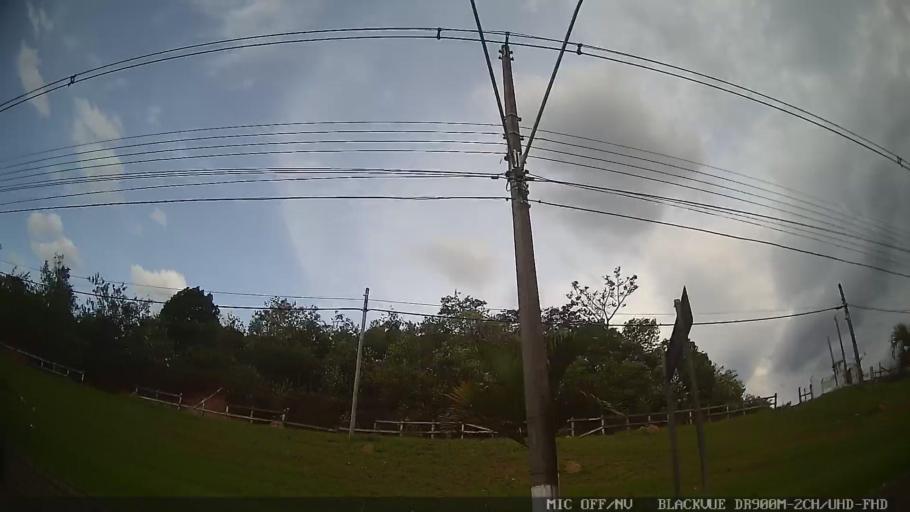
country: BR
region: Sao Paulo
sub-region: Itatiba
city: Itatiba
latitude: -22.8861
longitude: -46.7913
